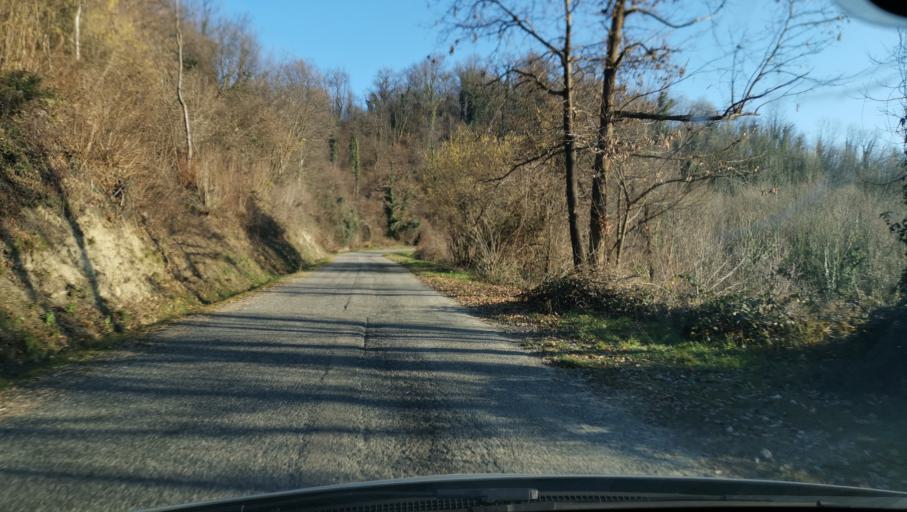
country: IT
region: Piedmont
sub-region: Provincia di Torino
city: Castagneto Po
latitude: 45.1379
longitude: 7.8904
